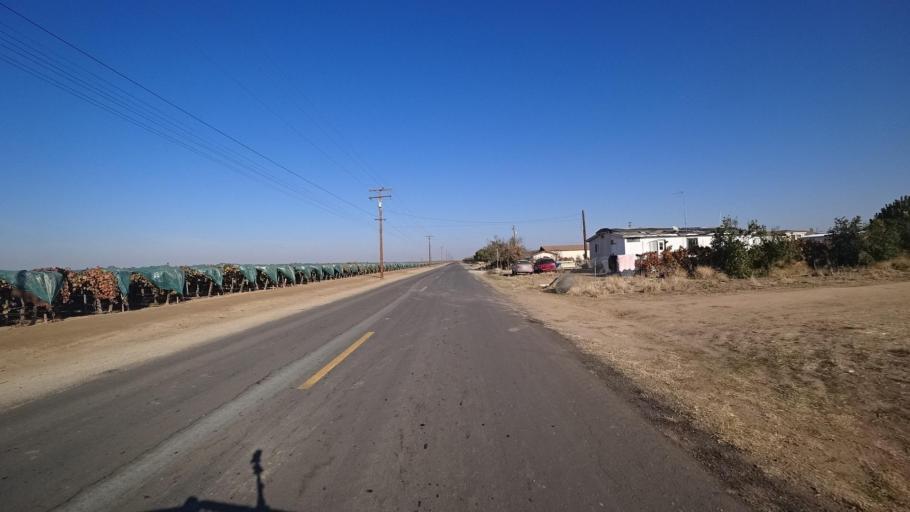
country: US
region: California
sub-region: Tulare County
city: Richgrove
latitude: 35.7526
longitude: -119.1338
